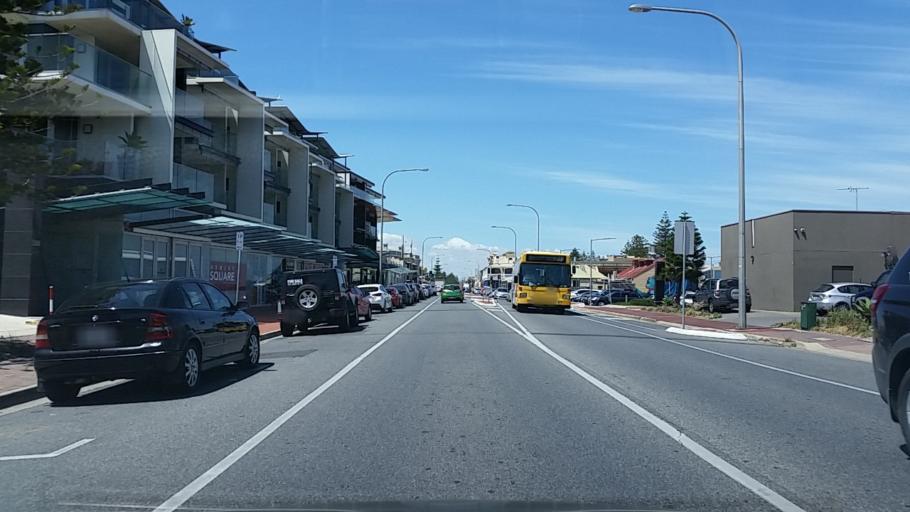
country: AU
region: South Australia
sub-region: Charles Sturt
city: Henley Beach
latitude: -34.9182
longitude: 138.4940
